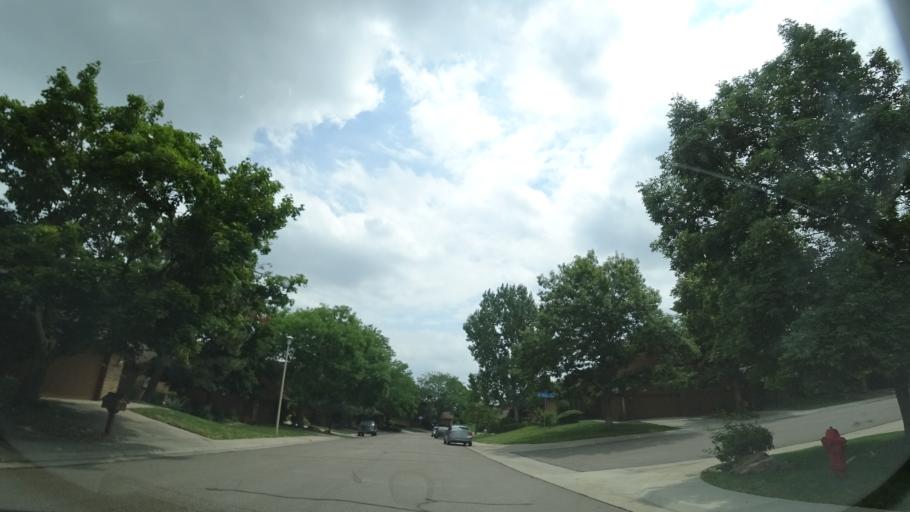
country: US
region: Colorado
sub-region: Jefferson County
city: West Pleasant View
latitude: 39.7198
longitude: -105.1442
